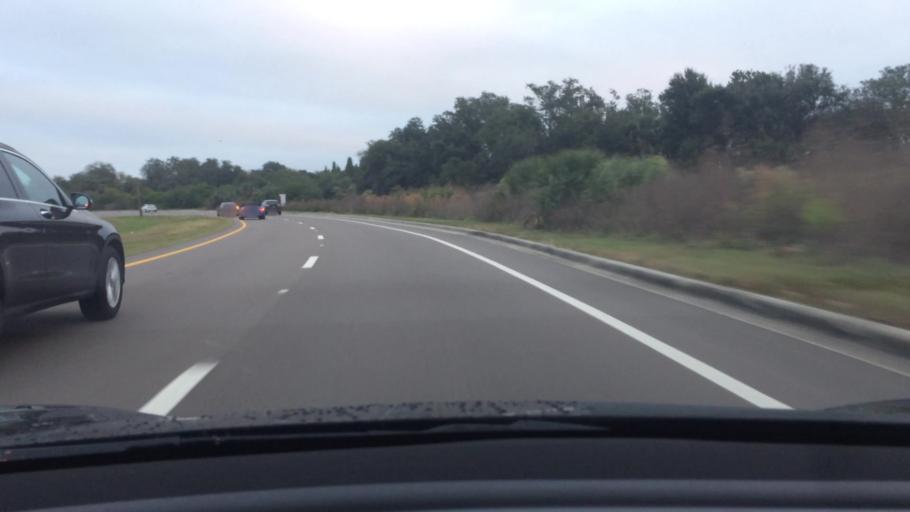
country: US
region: Florida
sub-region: Hillsborough County
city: Progress Village
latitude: 27.8925
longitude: -82.3575
